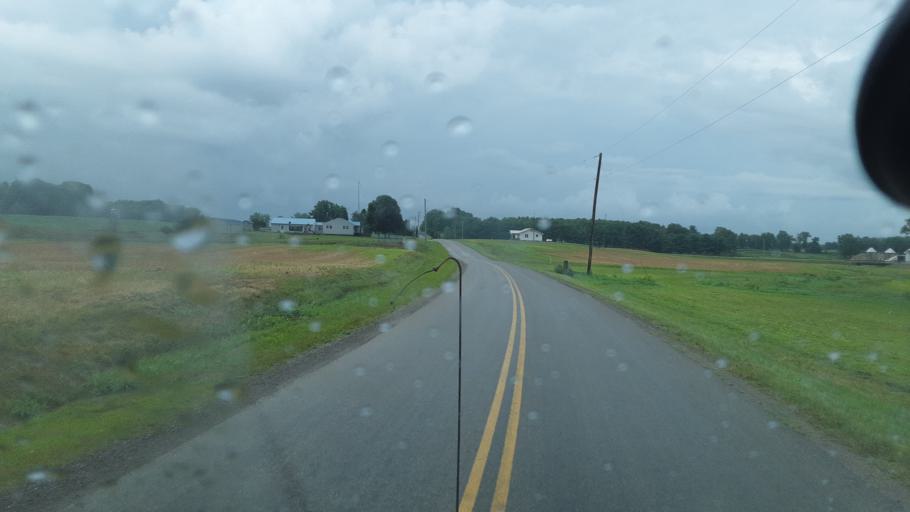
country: US
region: Indiana
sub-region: Steuben County
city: Fremont
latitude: 41.6565
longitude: -84.7956
